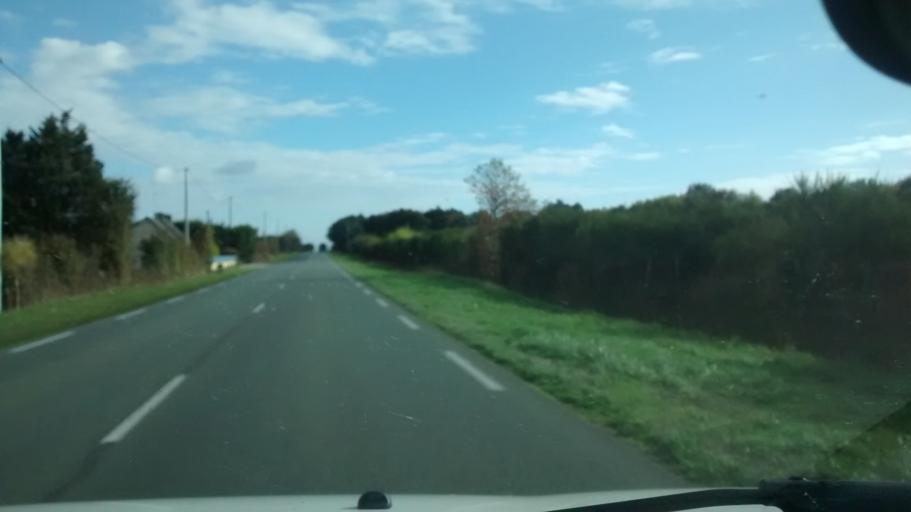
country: FR
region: Pays de la Loire
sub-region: Departement de Maine-et-Loire
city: Pouance
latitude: 47.7445
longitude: -1.2369
